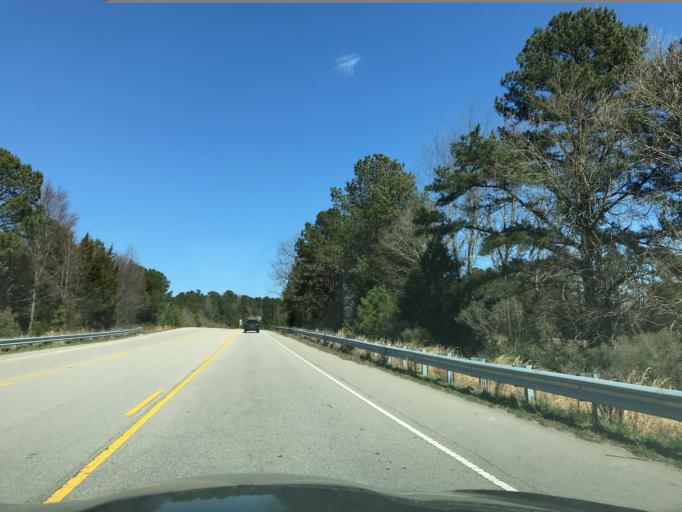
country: US
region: North Carolina
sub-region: Wake County
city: Wake Forest
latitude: 35.9675
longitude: -78.5604
